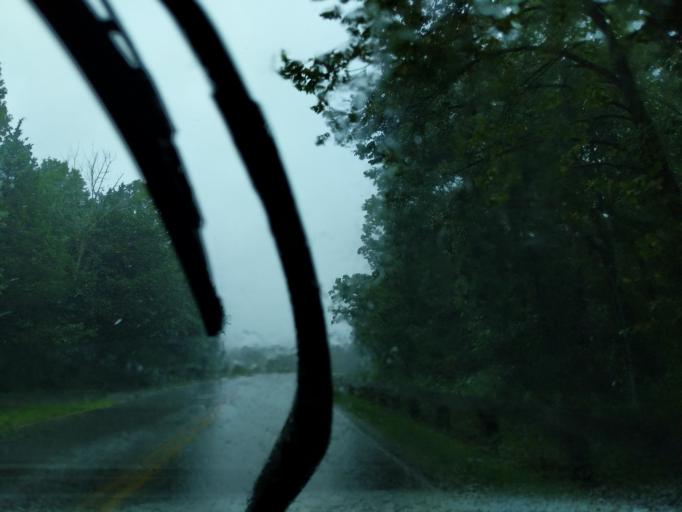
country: US
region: Kentucky
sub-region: Barren County
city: Cave City
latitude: 37.1513
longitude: -86.0980
